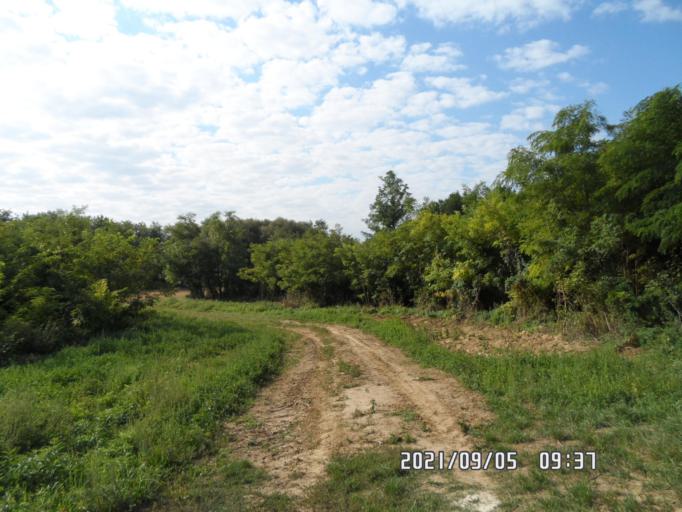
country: HU
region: Somogy
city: Bohonye
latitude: 46.4975
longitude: 17.3492
